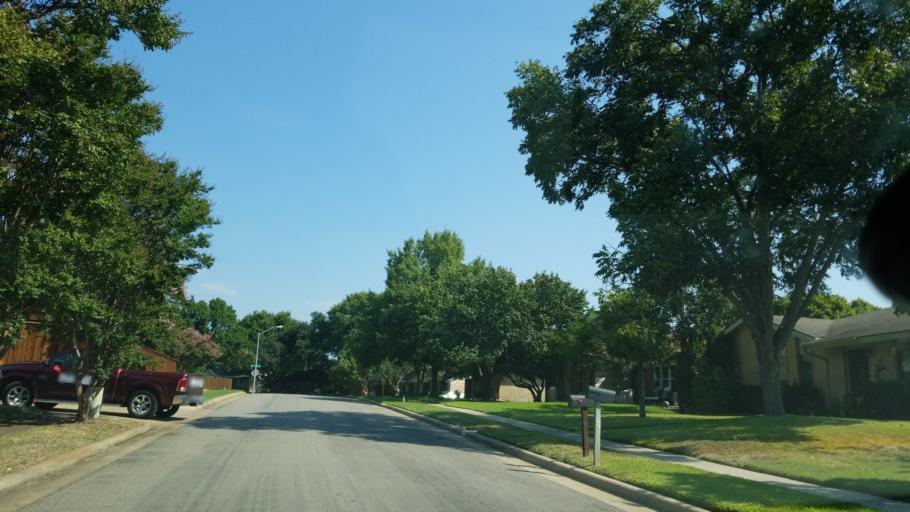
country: US
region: Texas
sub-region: Dallas County
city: Garland
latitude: 32.8732
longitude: -96.6948
